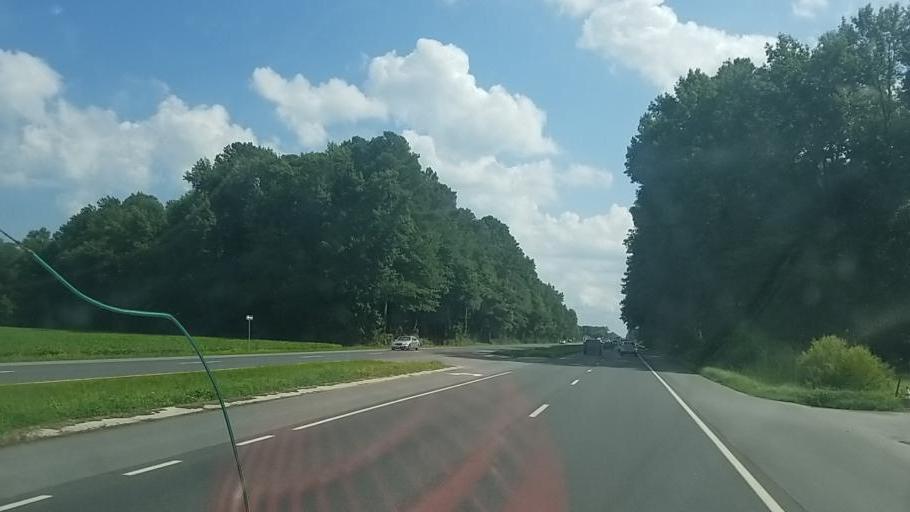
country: US
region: Delaware
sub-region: Sussex County
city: Selbyville
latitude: 38.5066
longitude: -75.2379
